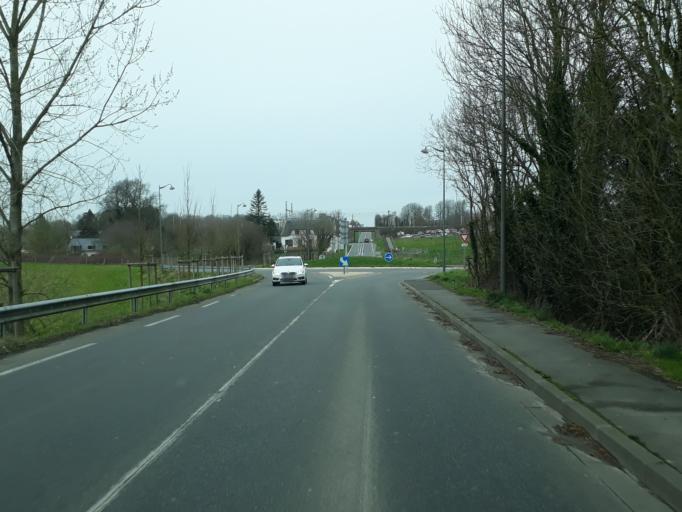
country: FR
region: Haute-Normandie
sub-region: Departement de la Seine-Maritime
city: Beuzeville-la-Grenier
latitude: 49.6007
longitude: 0.4174
